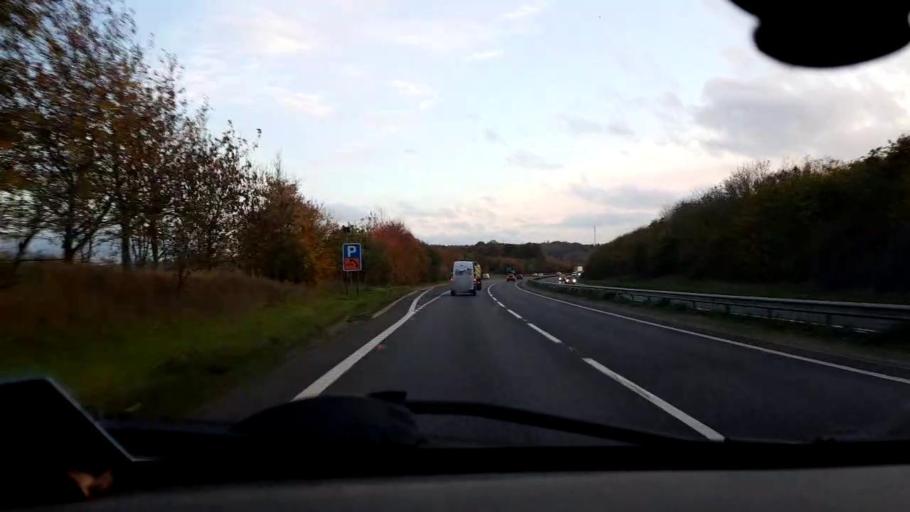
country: GB
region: England
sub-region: Norfolk
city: Bowthorpe
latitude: 52.6385
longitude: 1.1950
